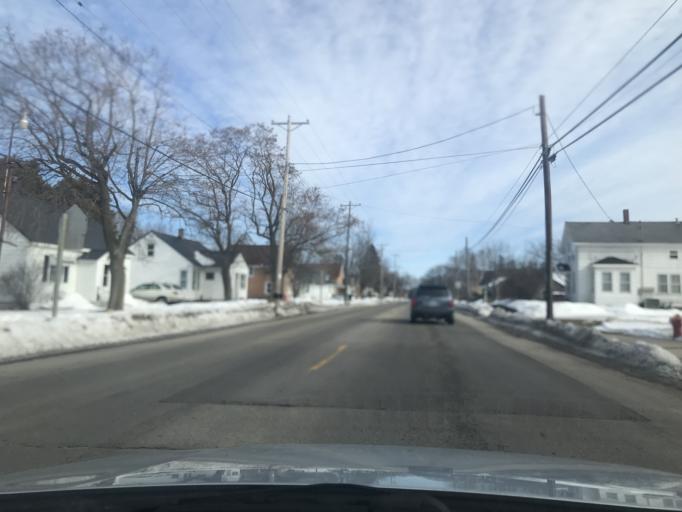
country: US
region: Wisconsin
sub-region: Oconto County
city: Gillett
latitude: 44.8882
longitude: -88.3128
